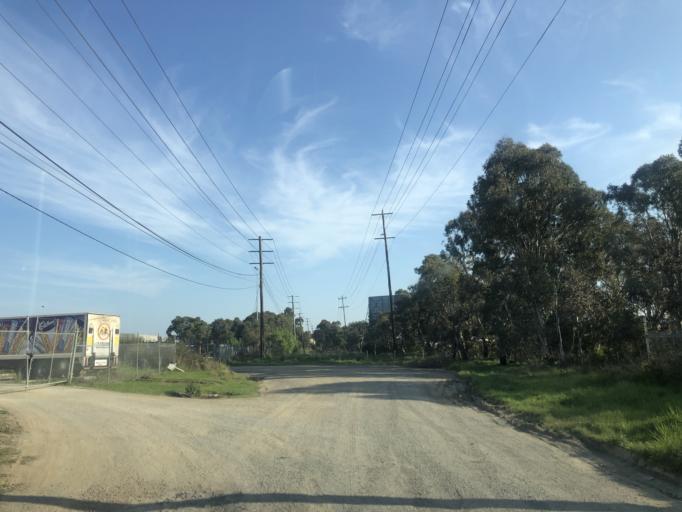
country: AU
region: Victoria
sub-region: Casey
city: Doveton
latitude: -38.0092
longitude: 145.2351
